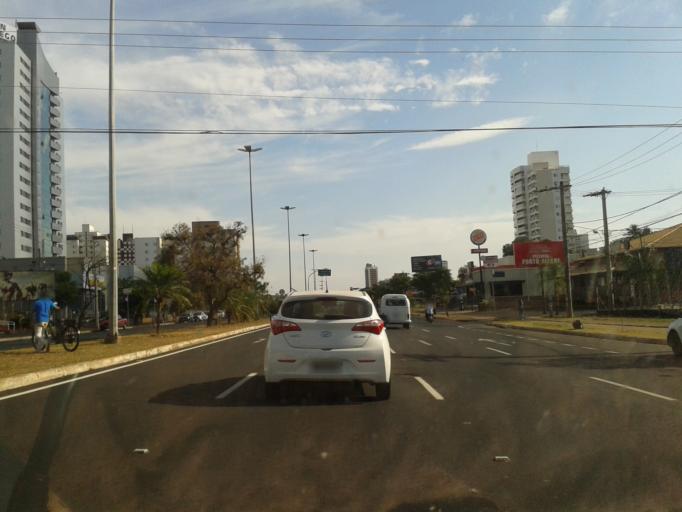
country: BR
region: Minas Gerais
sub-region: Uberlandia
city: Uberlandia
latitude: -18.9162
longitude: -48.2642
